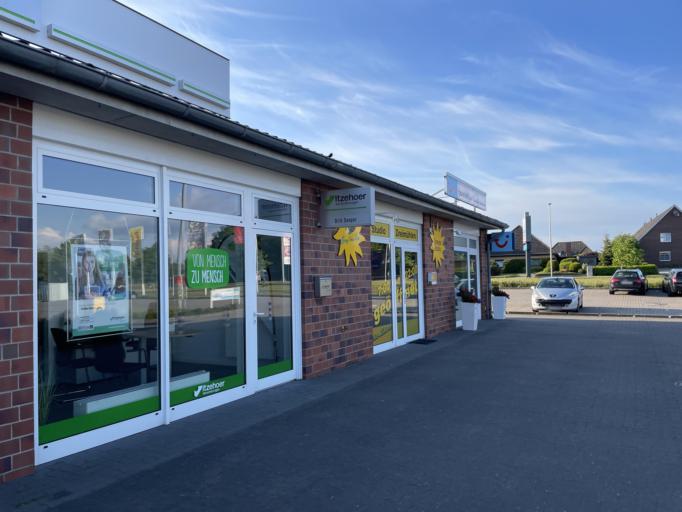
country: DE
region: Schleswig-Holstein
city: Mildstedt
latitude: 54.4703
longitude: 9.0898
